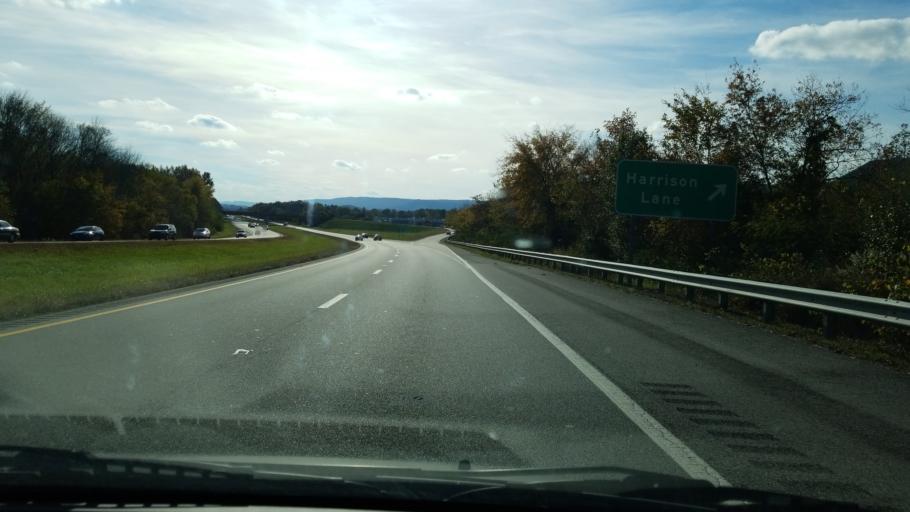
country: US
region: Tennessee
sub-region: Hamilton County
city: Soddy-Daisy
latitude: 35.2380
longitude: -85.1926
